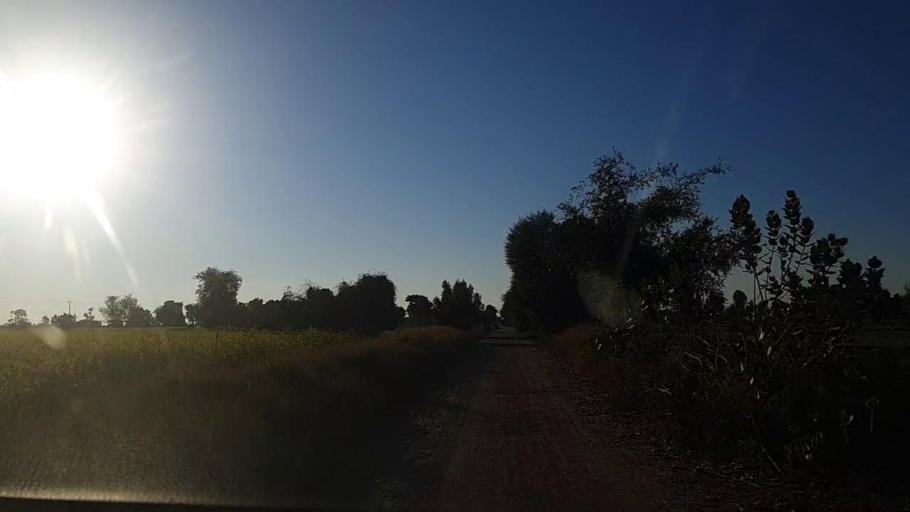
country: PK
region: Sindh
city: Sanghar
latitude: 26.1480
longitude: 68.9198
